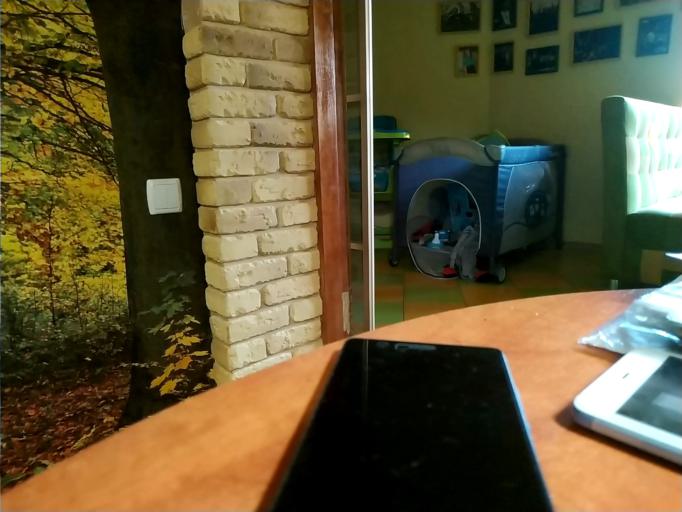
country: RU
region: Kaluga
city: Seredeyskiy
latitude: 53.7534
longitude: 35.4111
